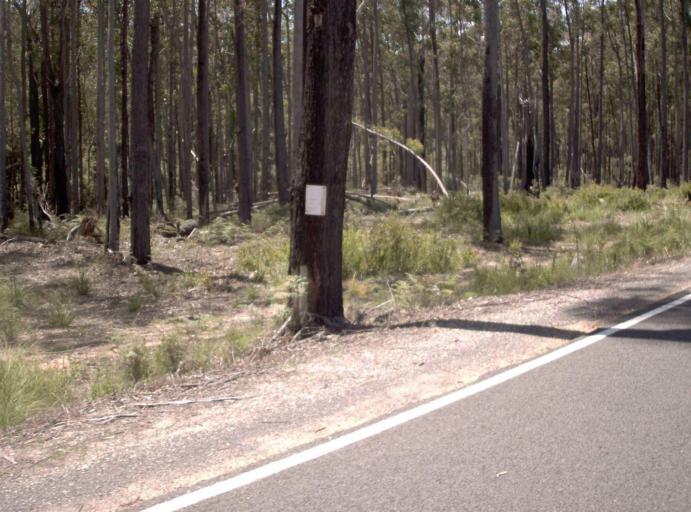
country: AU
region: Victoria
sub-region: East Gippsland
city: Lakes Entrance
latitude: -37.6723
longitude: 148.7944
